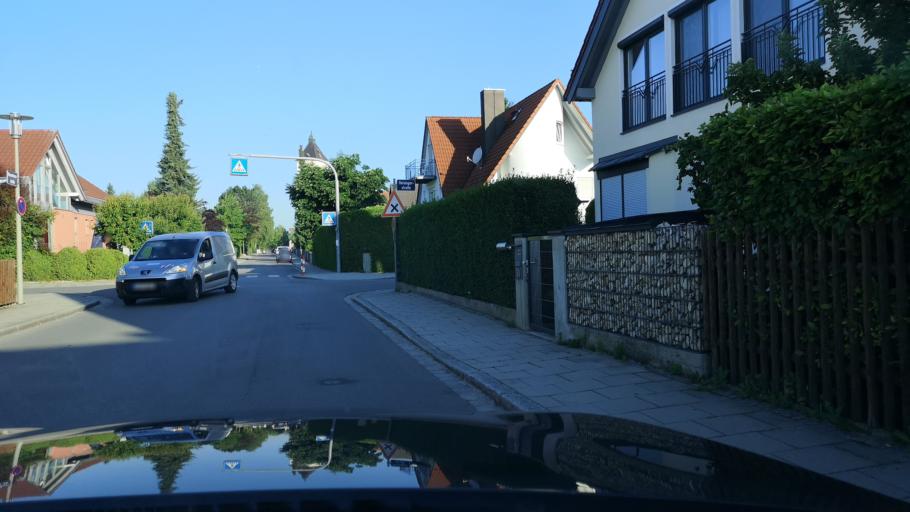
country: DE
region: Bavaria
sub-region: Upper Bavaria
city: Ismaning
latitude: 48.2202
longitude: 11.6698
